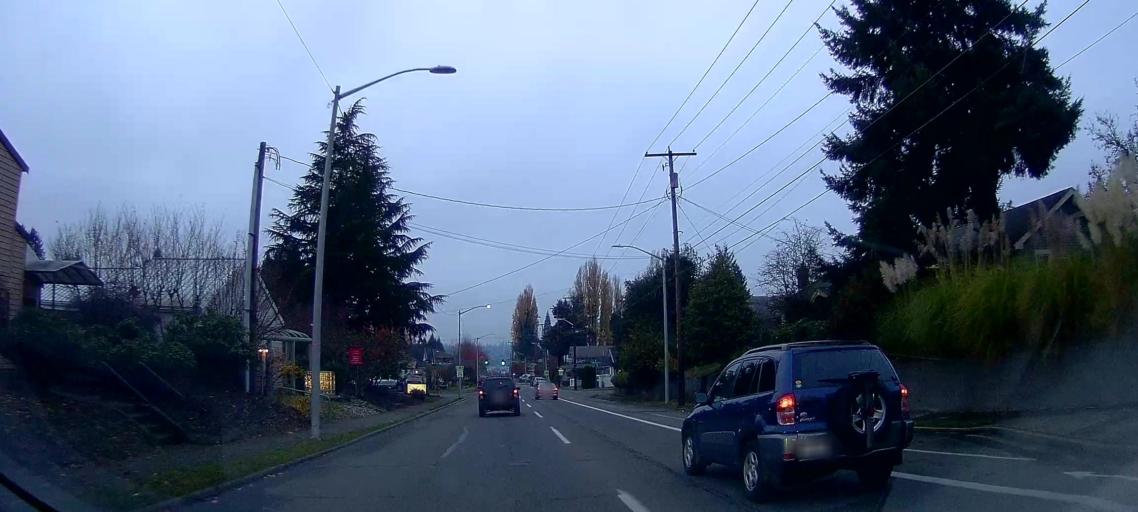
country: US
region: Washington
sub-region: Thurston County
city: Olympia
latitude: 47.0469
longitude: -122.8796
